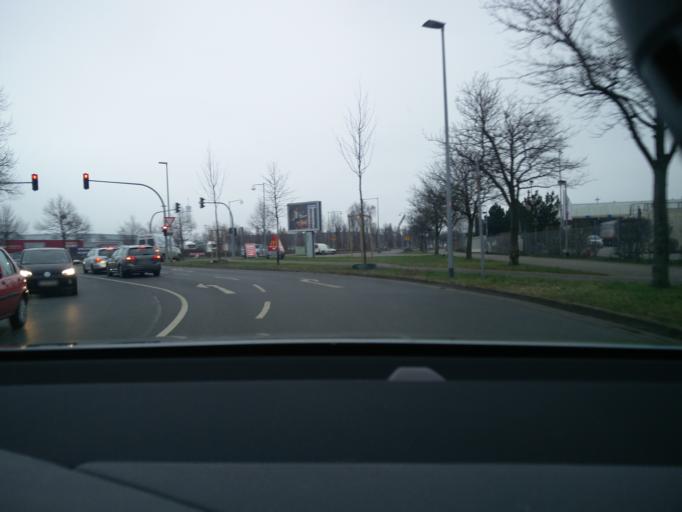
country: DE
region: Lower Saxony
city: Laatzen
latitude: 52.3268
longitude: 9.7923
